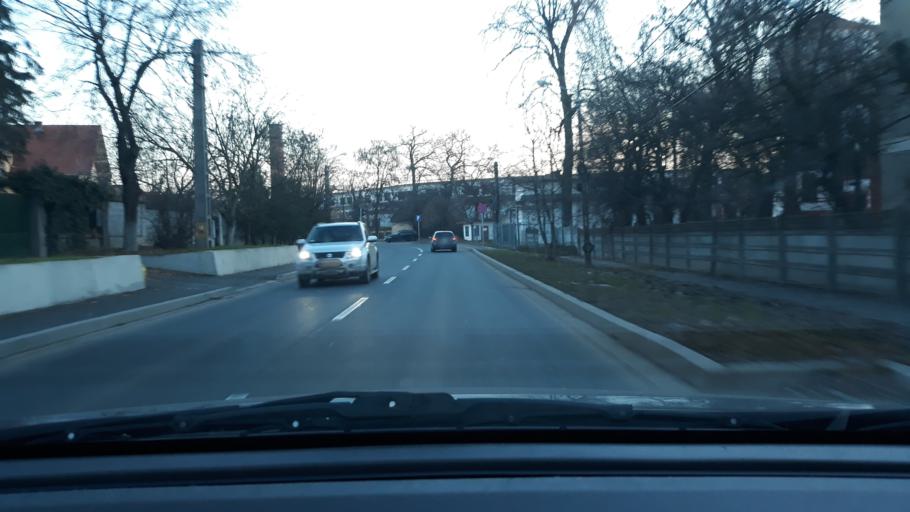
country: RO
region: Bihor
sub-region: Comuna Biharea
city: Oradea
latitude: 47.0829
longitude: 21.9274
